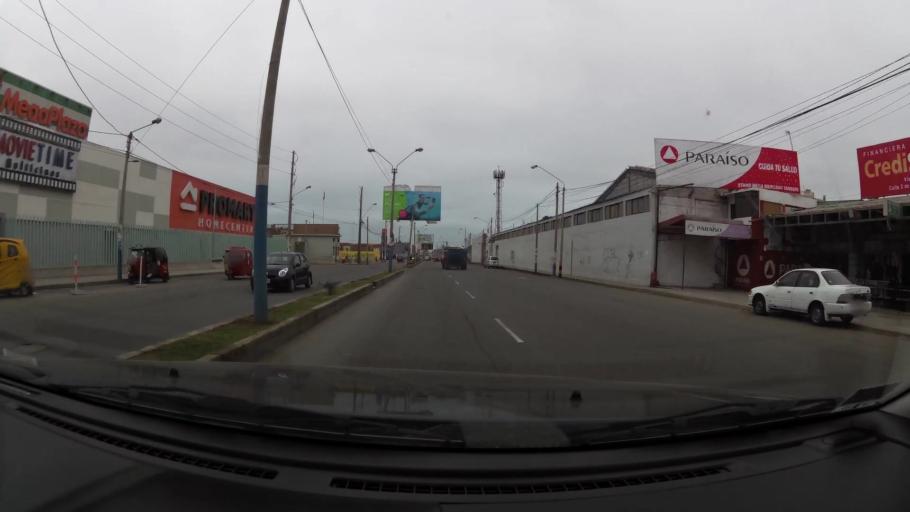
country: PE
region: Ica
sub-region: Provincia de Pisco
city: Pisco
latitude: -13.7109
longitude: -76.1954
